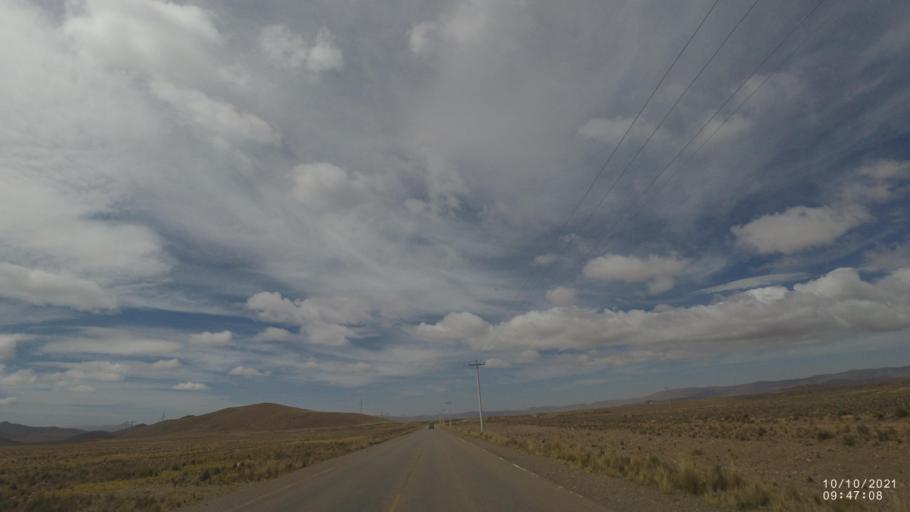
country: BO
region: La Paz
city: Quime
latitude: -17.1895
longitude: -67.3407
